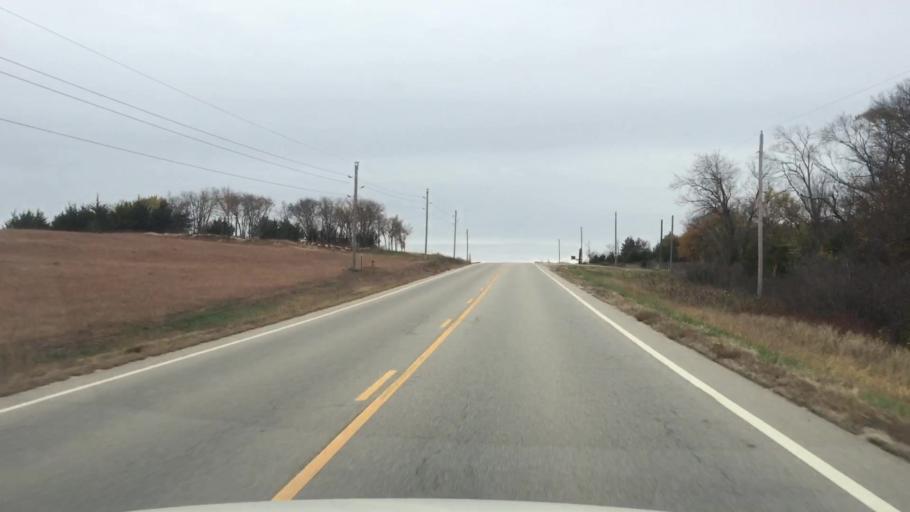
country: US
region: Kansas
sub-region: Pottawatomie County
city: Wamego
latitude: 39.1341
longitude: -96.3015
